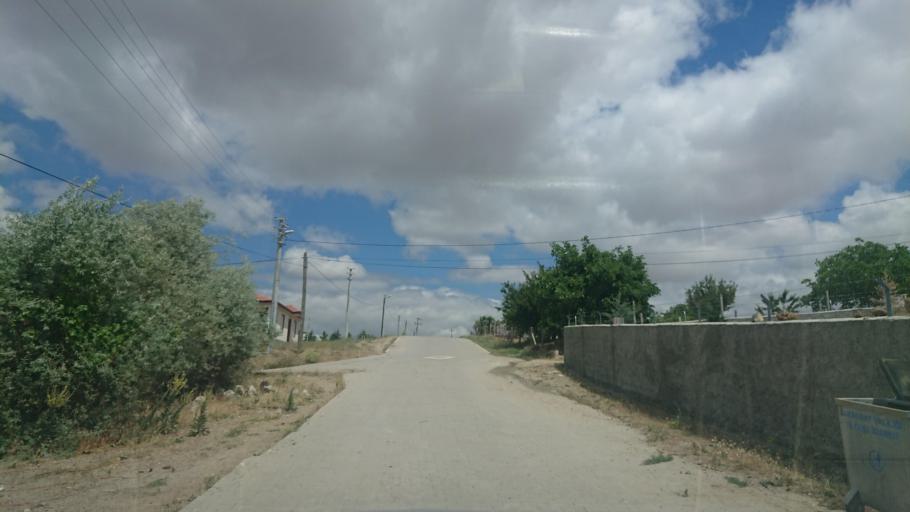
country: TR
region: Aksaray
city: Agacoren
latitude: 38.8679
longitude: 33.9469
